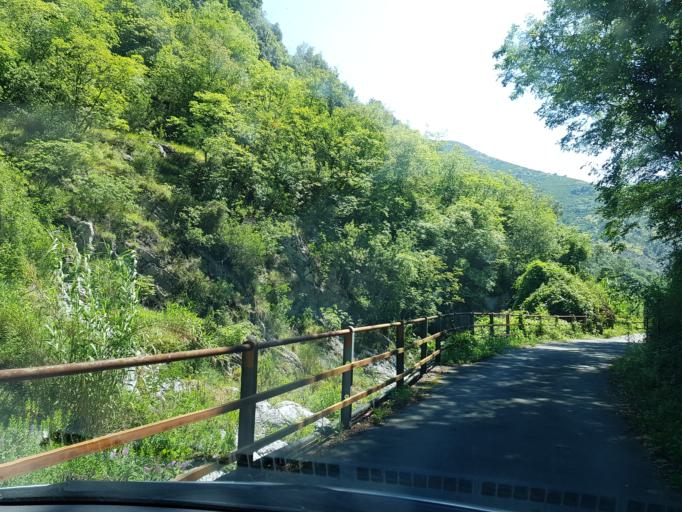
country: IT
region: Liguria
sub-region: Provincia di Genova
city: Genoa
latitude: 44.4486
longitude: 8.8498
